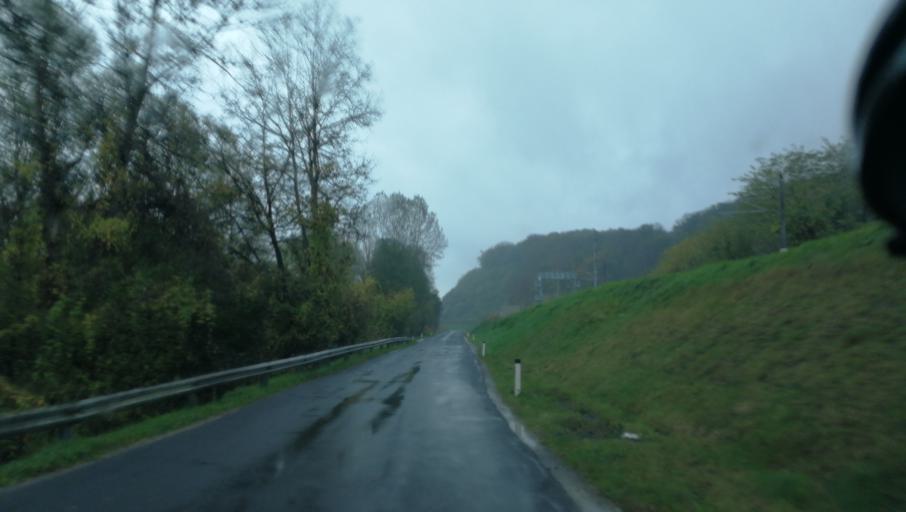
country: AT
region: Styria
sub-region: Politischer Bezirk Leibnitz
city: Ehrenhausen
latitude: 46.7266
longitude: 15.5904
